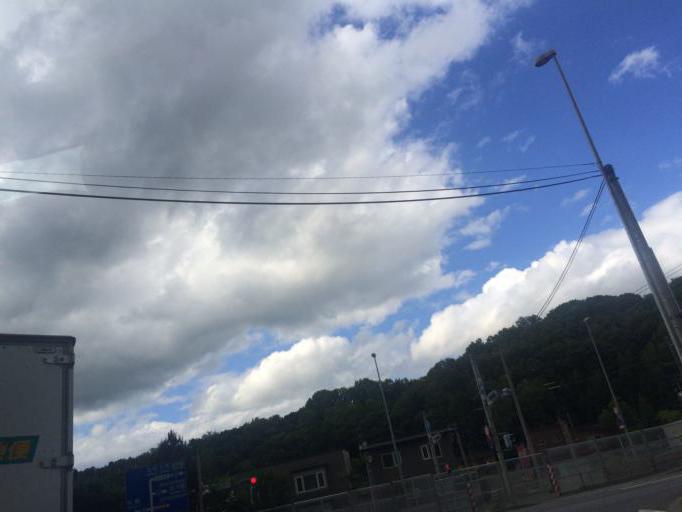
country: JP
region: Hokkaido
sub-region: Asahikawa-shi
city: Asahikawa
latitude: 43.7684
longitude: 142.2984
